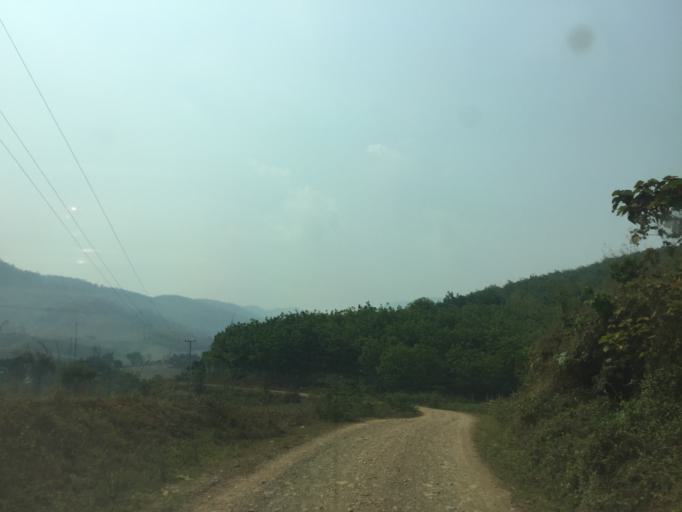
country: TH
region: Phayao
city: Phu Sang
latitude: 19.5732
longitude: 100.5254
